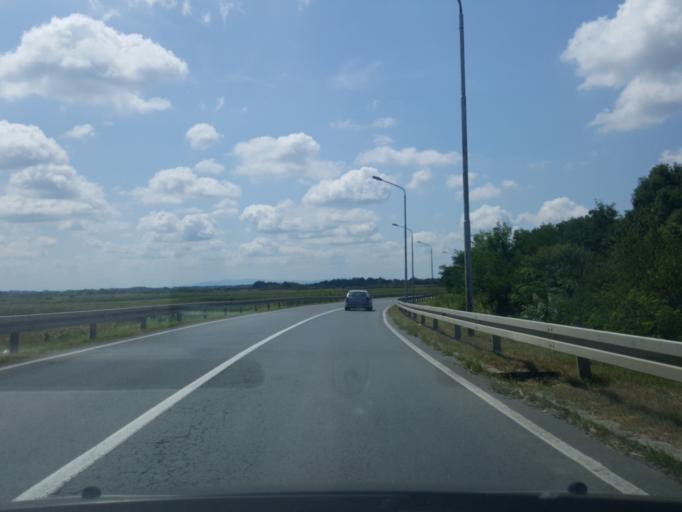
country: RS
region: Autonomna Pokrajina Vojvodina
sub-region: Sremski Okrug
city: Sremska Mitrovica
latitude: 44.9539
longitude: 19.6316
